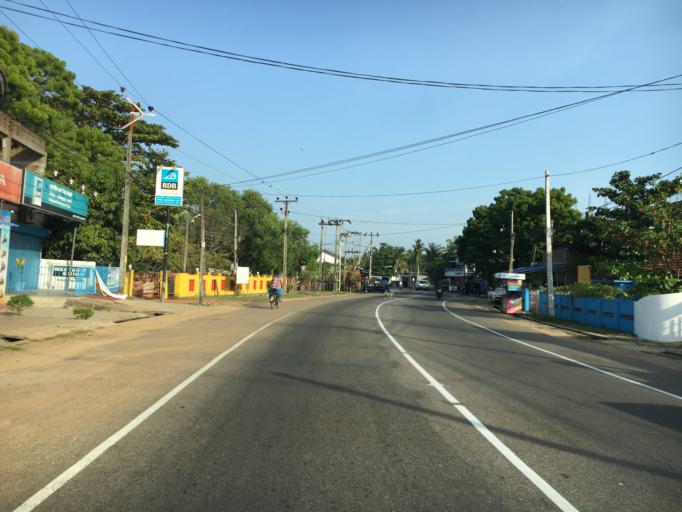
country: LK
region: Eastern Province
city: Eravur Town
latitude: 7.9100
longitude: 81.5304
